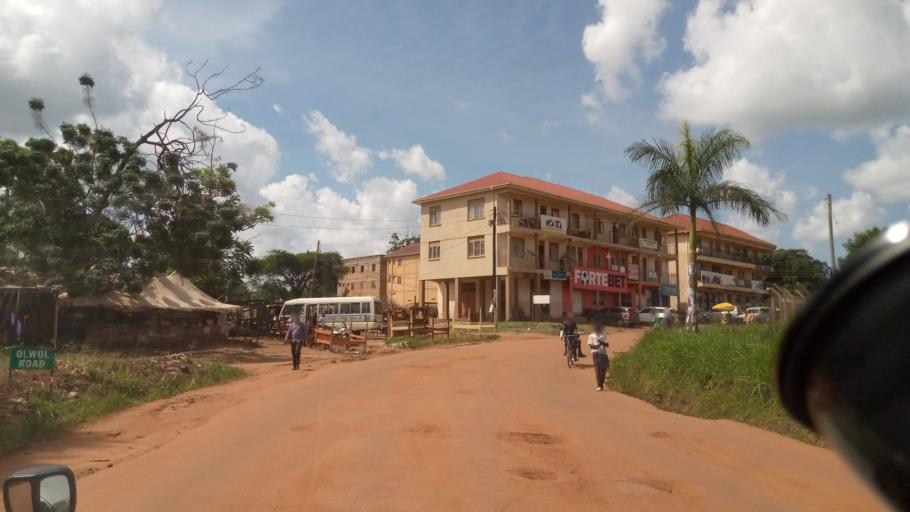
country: UG
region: Northern Region
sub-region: Lira District
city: Lira
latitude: 2.2469
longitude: 32.8977
